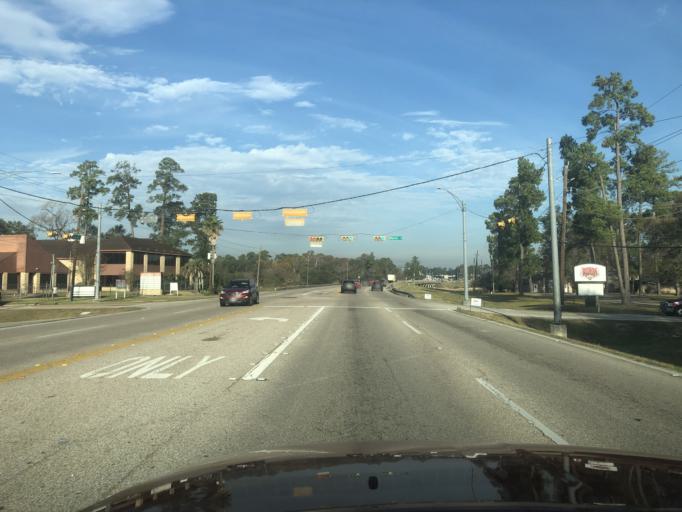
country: US
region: Texas
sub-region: Harris County
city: Spring
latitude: 30.0220
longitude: -95.4745
